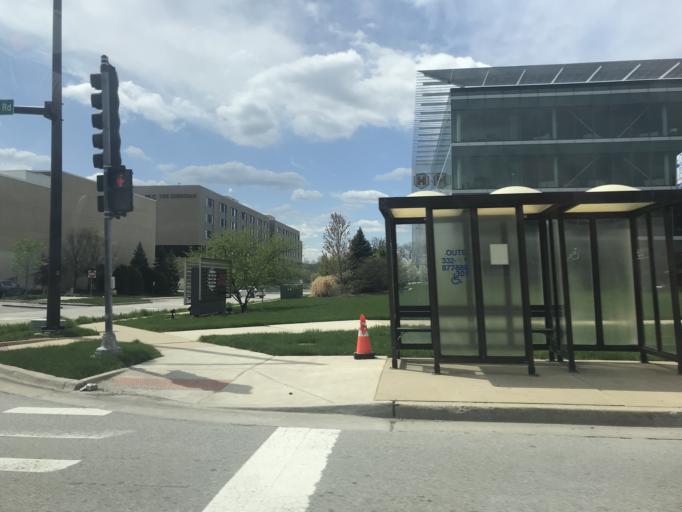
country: US
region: Illinois
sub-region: DuPage County
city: Oak Brook
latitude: 41.8502
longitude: -87.9294
